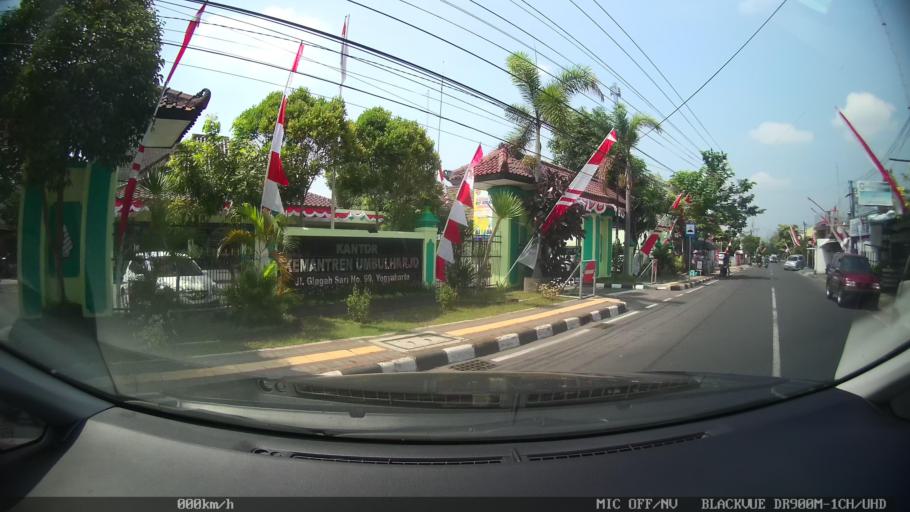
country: ID
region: Daerah Istimewa Yogyakarta
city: Yogyakarta
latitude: -7.8096
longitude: 110.3874
